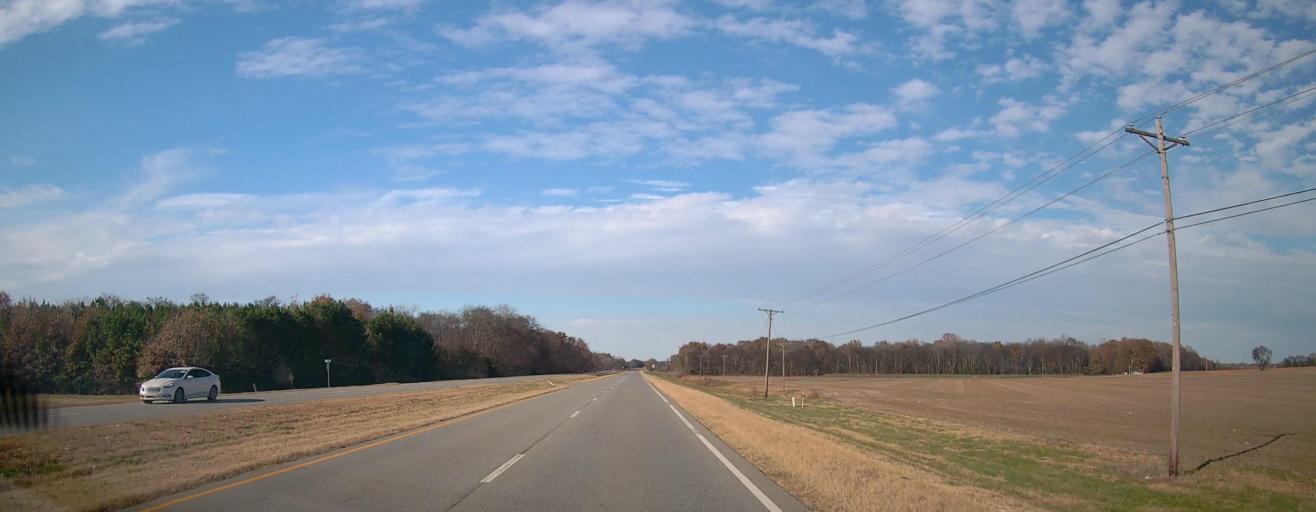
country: US
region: Alabama
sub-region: Morgan County
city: Decatur
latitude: 34.6832
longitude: -86.9505
